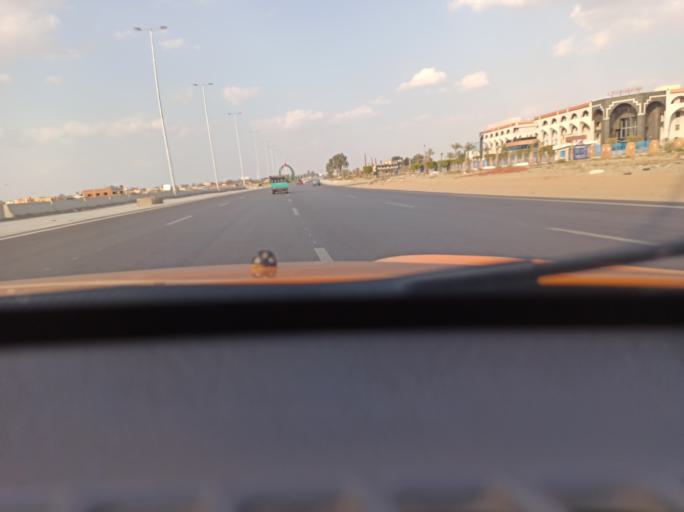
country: EG
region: Al Isma'iliyah
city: Ismailia
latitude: 30.6042
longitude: 32.2112
